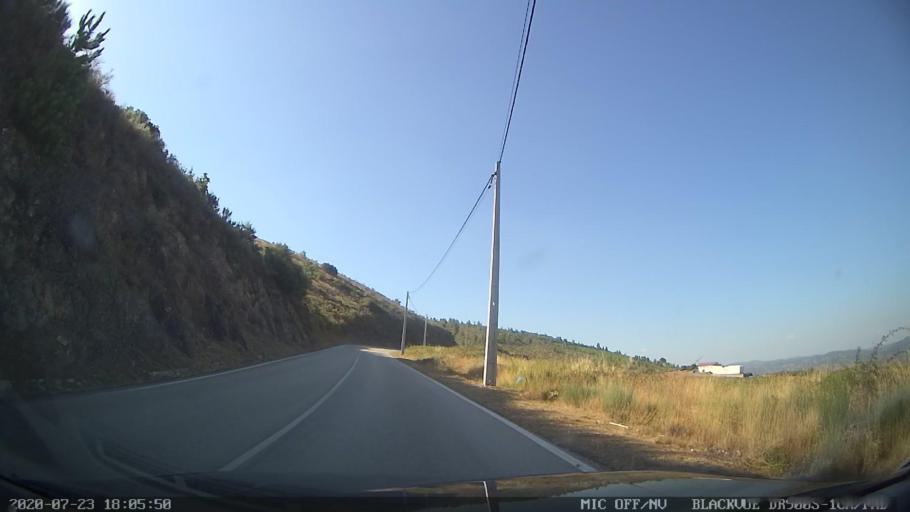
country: PT
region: Viseu
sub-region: Sao Joao da Pesqueira
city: Sao Joao da Pesqueira
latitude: 41.1573
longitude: -7.4363
